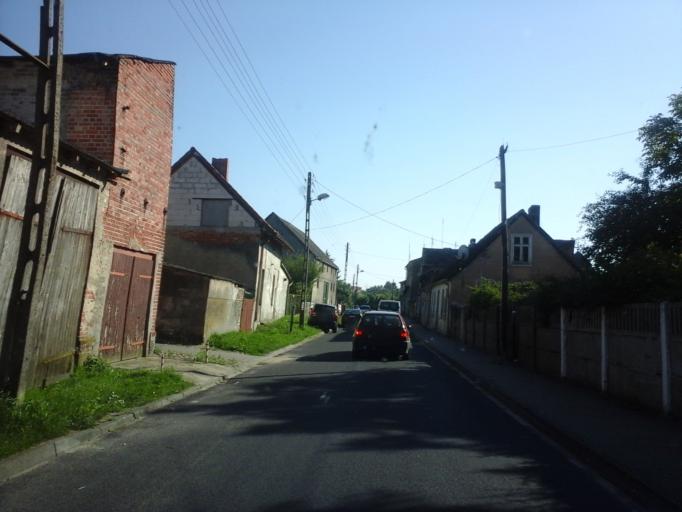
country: PL
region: West Pomeranian Voivodeship
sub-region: Powiat lobeski
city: Dobra
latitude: 53.5871
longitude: 15.3081
